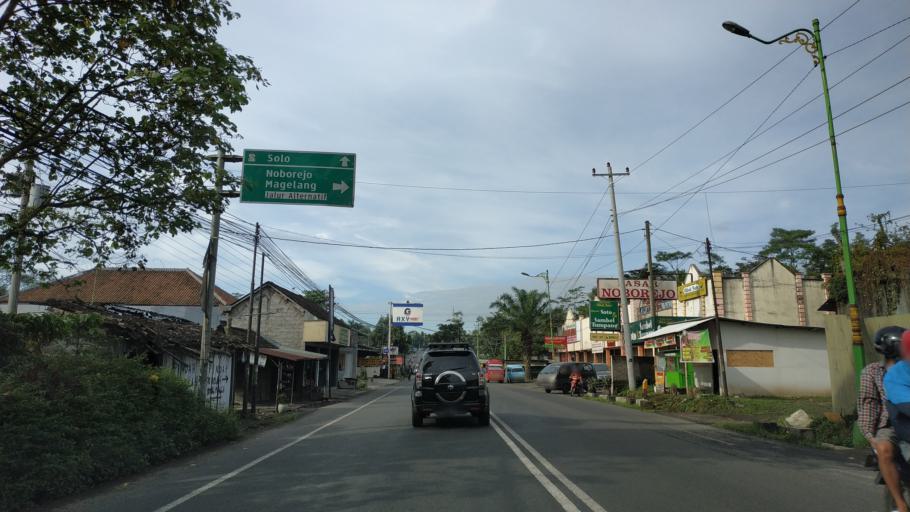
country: ID
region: Central Java
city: Salatiga
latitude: -7.3839
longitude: 110.5150
